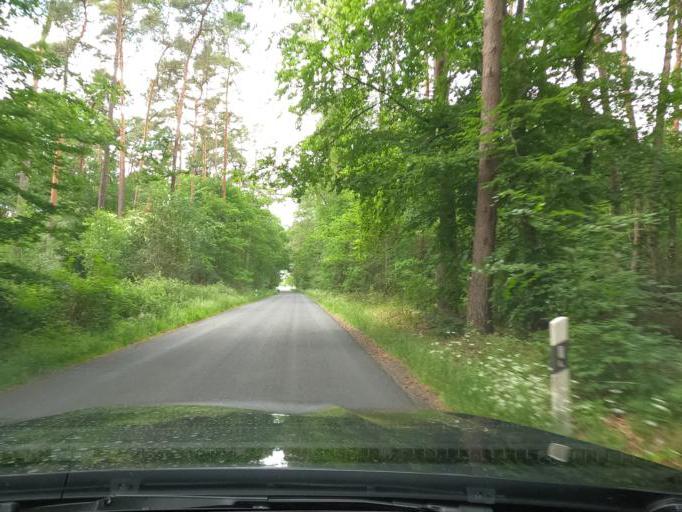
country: DE
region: Lower Saxony
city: Steimbke
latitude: 52.6389
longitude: 9.4620
